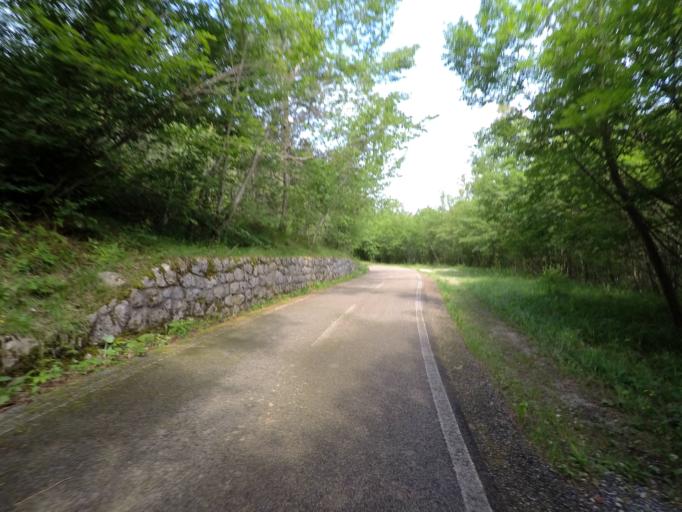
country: IT
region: Friuli Venezia Giulia
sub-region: Provincia di Udine
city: Amaro
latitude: 46.3603
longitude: 13.0911
